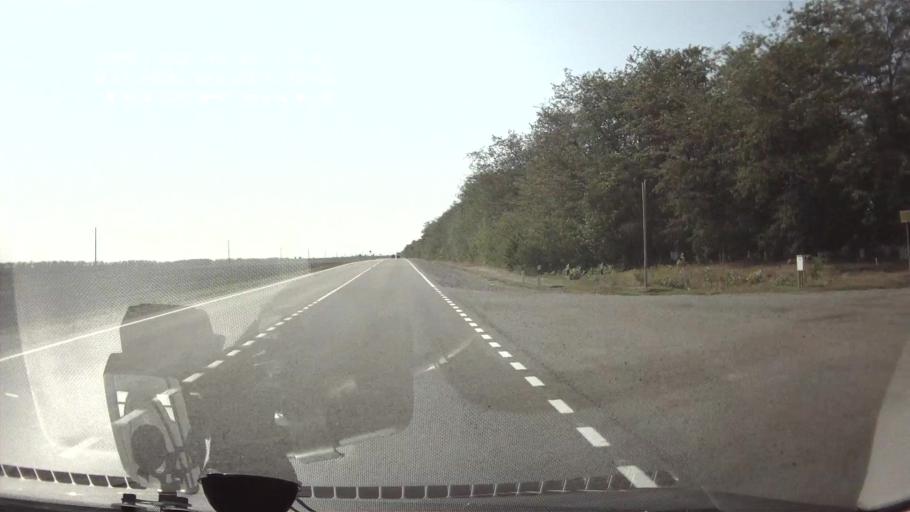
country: RU
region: Krasnodarskiy
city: Novopokrovskaya
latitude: 45.8986
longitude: 40.7210
